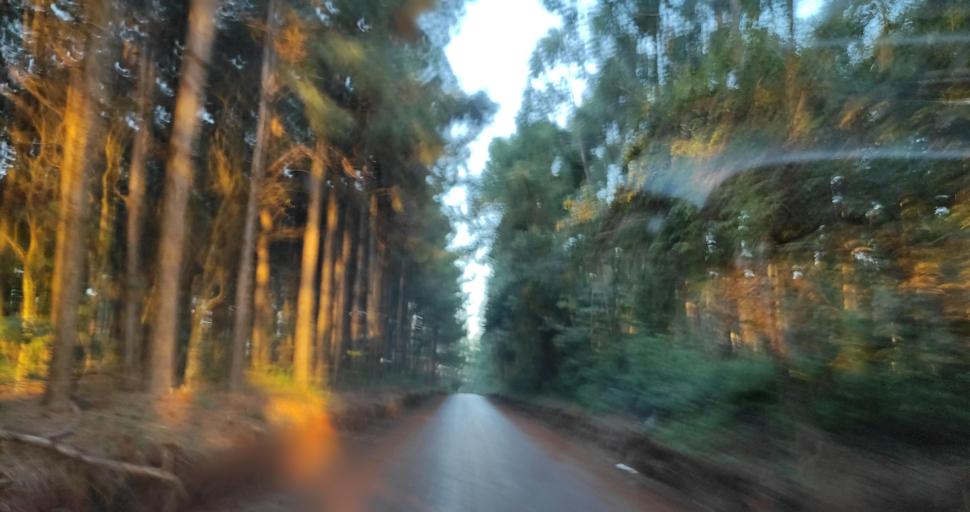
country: AR
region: Misiones
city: Capiovi
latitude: -26.8859
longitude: -55.0820
